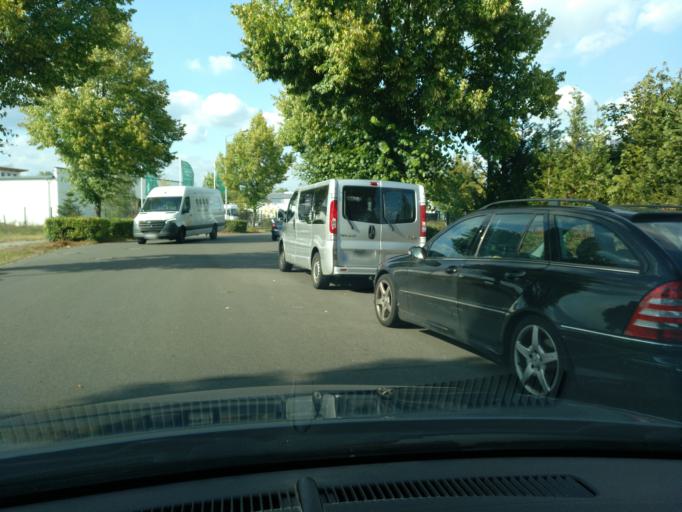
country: DE
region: Berlin
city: Mahlsdorf
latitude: 52.5059
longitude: 13.6322
